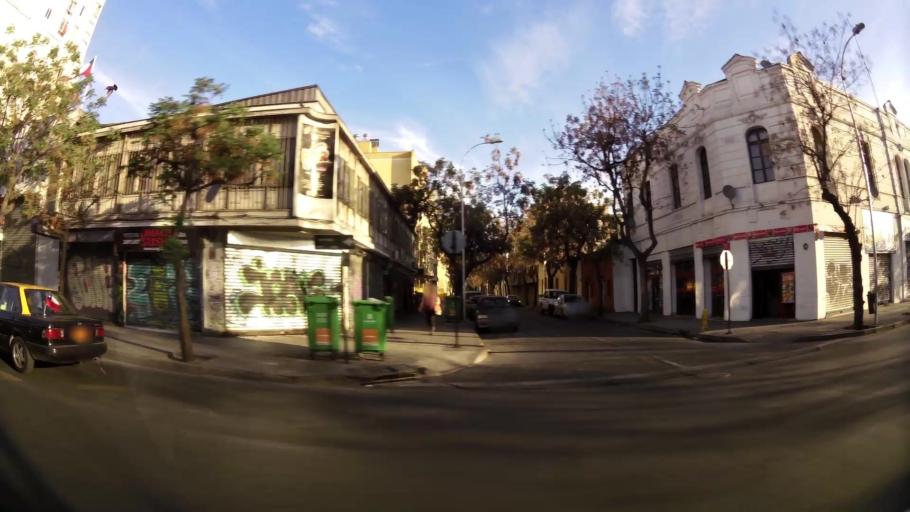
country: CL
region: Santiago Metropolitan
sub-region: Provincia de Santiago
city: Santiago
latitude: -33.4355
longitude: -70.6770
